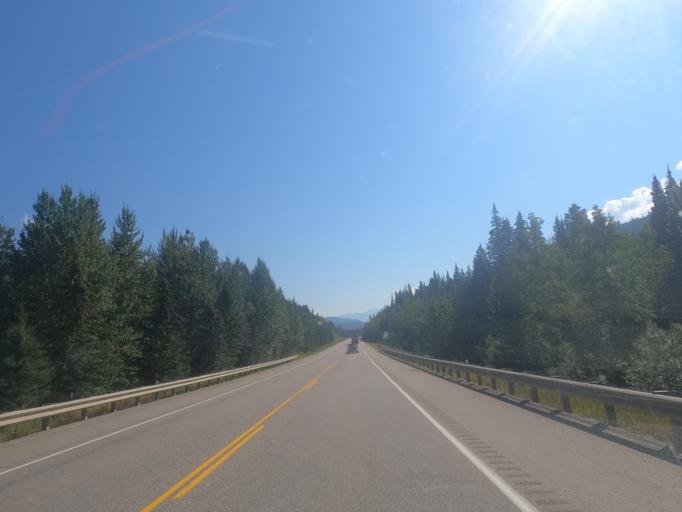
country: CA
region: Alberta
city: Jasper Park Lodge
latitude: 52.8765
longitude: -118.3275
